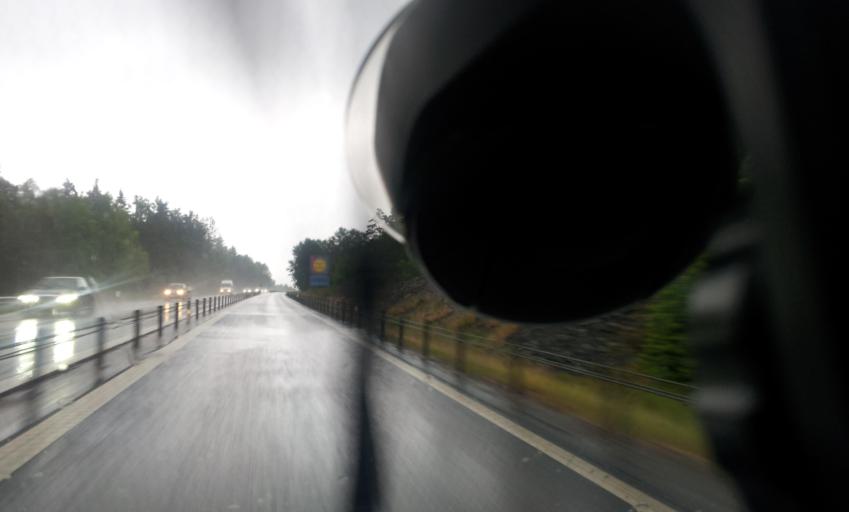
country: SE
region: Kalmar
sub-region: Oskarshamns Kommun
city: Oskarshamn
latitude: 57.2981
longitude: 16.4604
